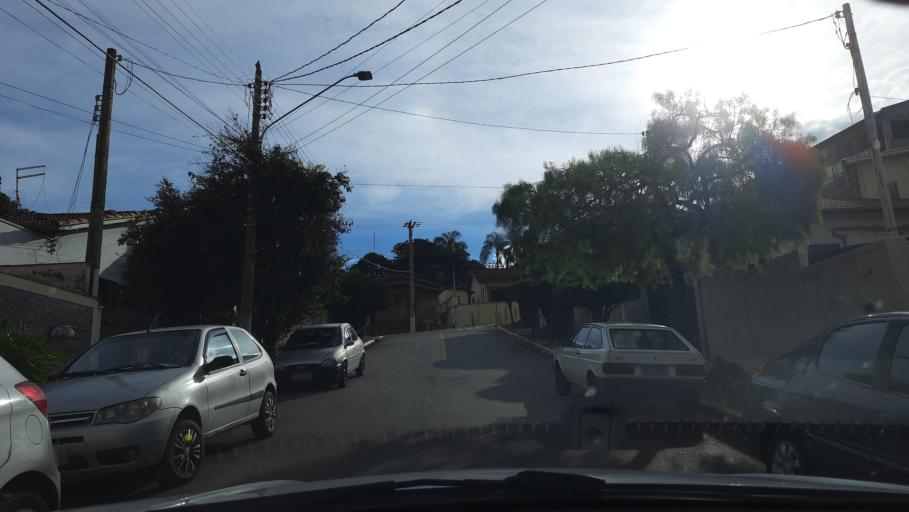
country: BR
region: Sao Paulo
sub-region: Sao Joao Da Boa Vista
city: Sao Joao da Boa Vista
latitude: -21.9458
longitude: -46.7147
